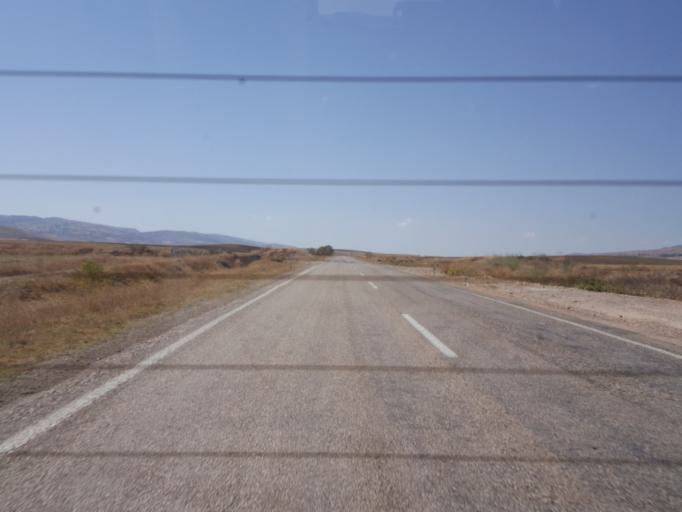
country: TR
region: Amasya
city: Dogantepe
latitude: 40.5754
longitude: 35.5971
